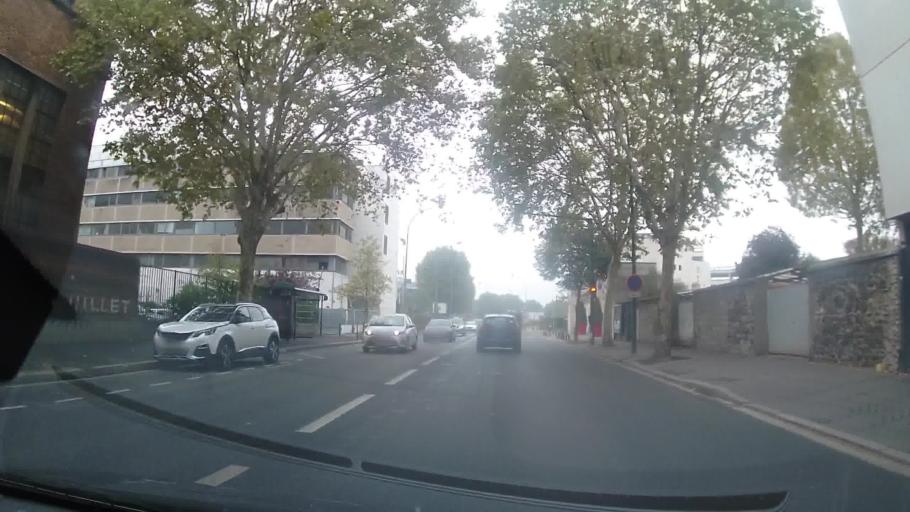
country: FR
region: Ile-de-France
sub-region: Departement des Hauts-de-Seine
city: Clichy
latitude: 48.9084
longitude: 2.3128
